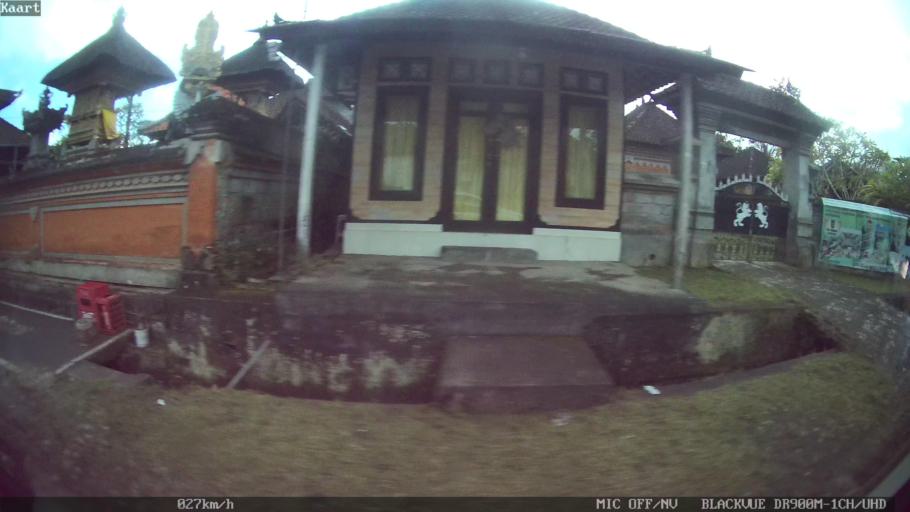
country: ID
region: Bali
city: Banjar Pesalakan
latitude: -8.5040
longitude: 115.3036
